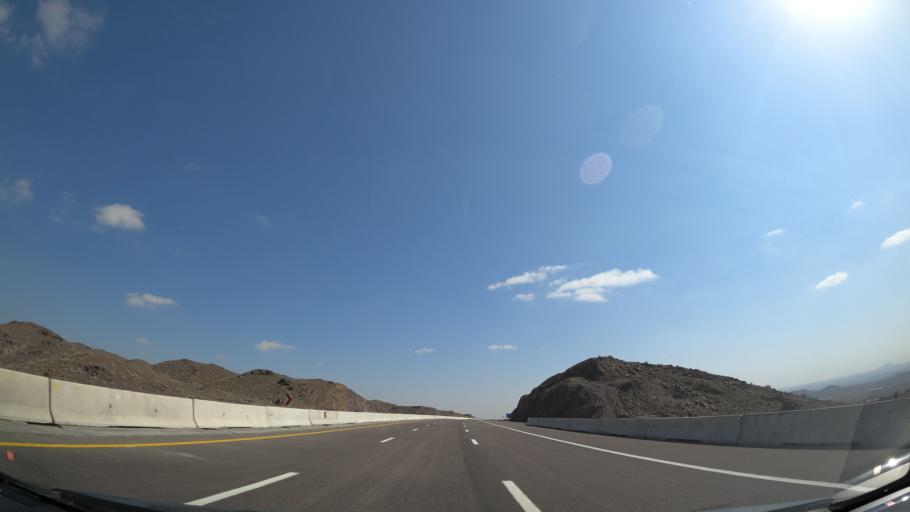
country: IR
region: Alborz
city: Nazarabad
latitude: 35.6599
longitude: 50.6591
